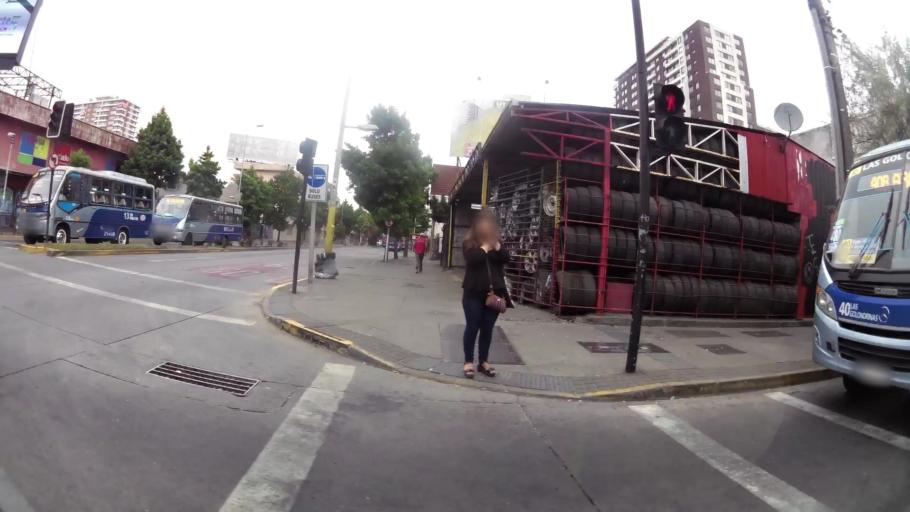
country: CL
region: Biobio
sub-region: Provincia de Concepcion
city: Concepcion
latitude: -36.8211
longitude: -73.0436
